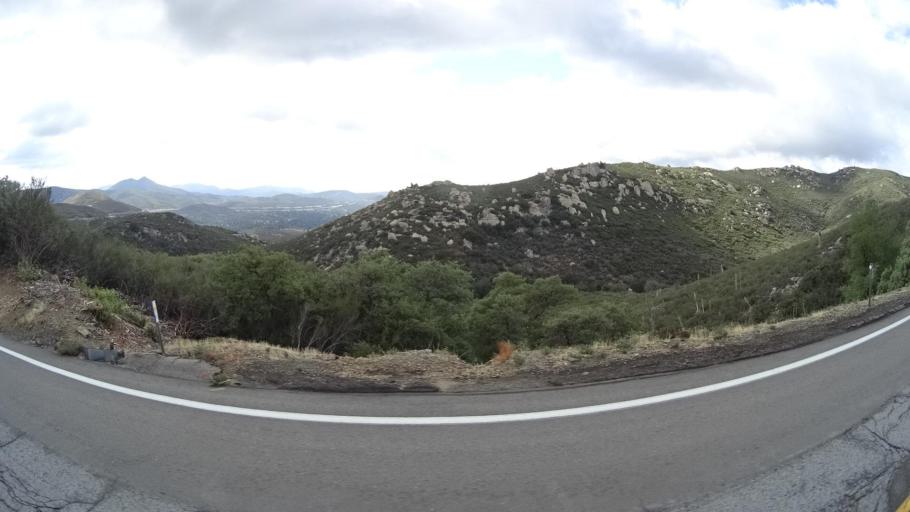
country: US
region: California
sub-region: San Diego County
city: Pine Valley
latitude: 32.8342
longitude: -116.4959
